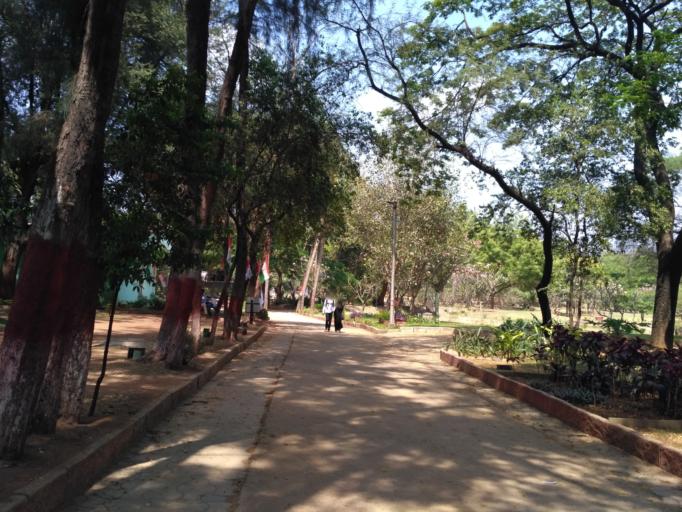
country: IN
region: Telangana
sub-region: Hyderabad
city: Hyderabad
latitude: 17.4135
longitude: 78.4812
